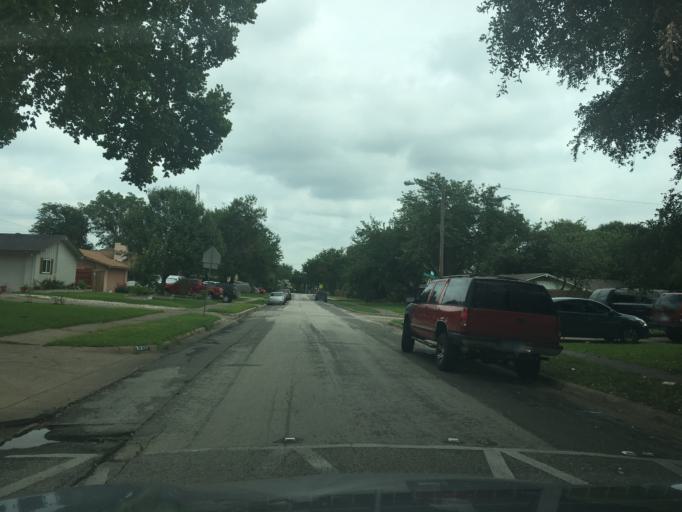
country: US
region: Texas
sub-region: Dallas County
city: Richardson
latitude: 32.9381
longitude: -96.7635
